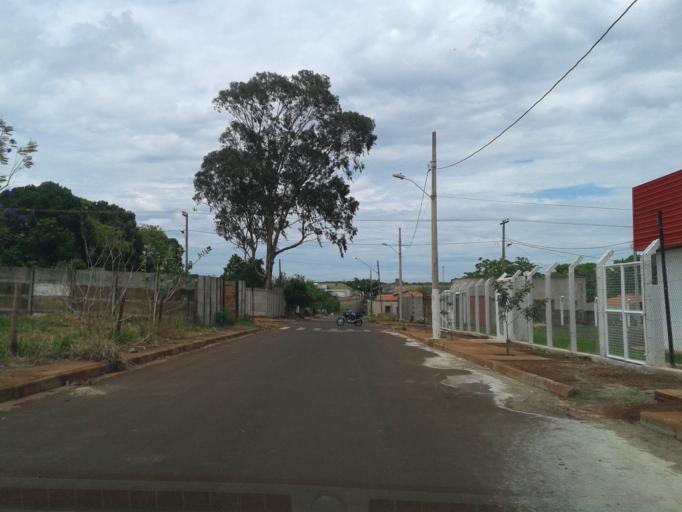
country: BR
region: Minas Gerais
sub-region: Ituiutaba
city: Ituiutaba
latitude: -18.9949
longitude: -49.4624
